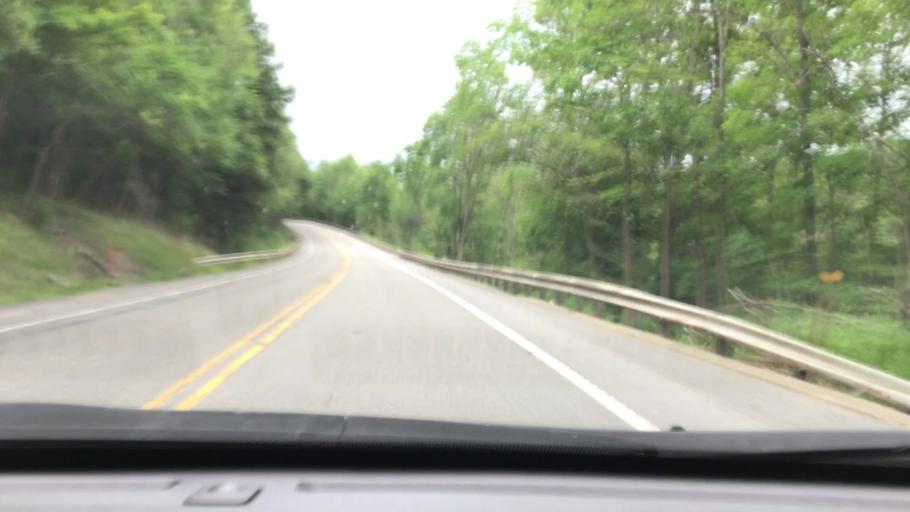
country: US
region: Pennsylvania
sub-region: McKean County
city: Bradford
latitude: 41.8551
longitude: -78.6745
